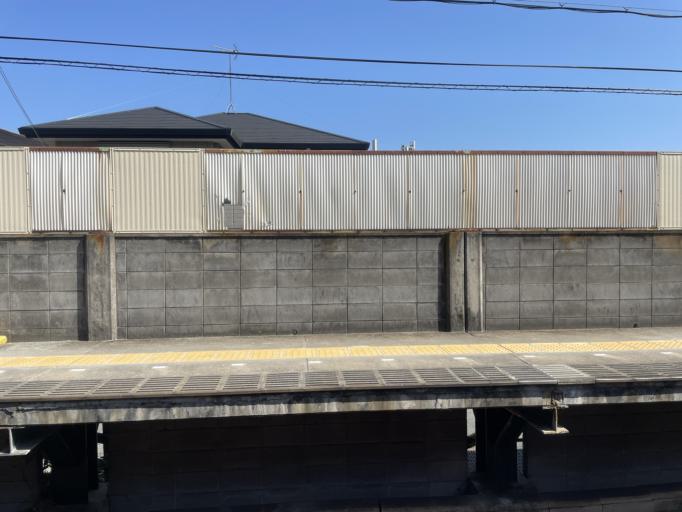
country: JP
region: Osaka
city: Kashihara
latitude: 34.6013
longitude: 135.6953
